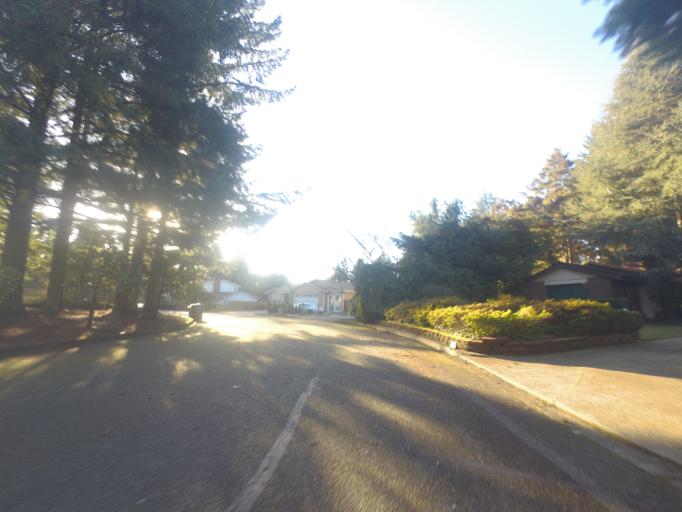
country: US
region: Washington
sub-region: Pierce County
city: Fircrest
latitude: 47.2231
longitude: -122.5189
